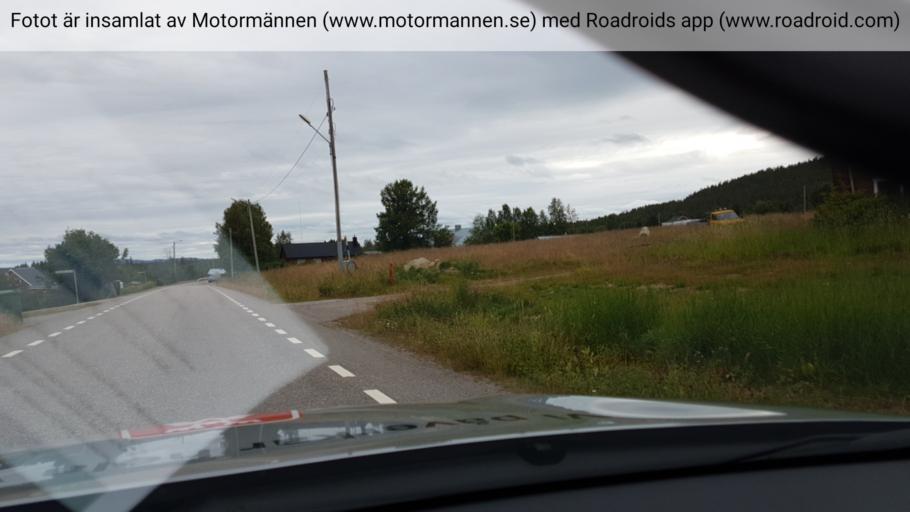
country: SE
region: Norrbotten
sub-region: Gallivare Kommun
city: Gaellivare
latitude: 67.0215
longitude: 21.8084
